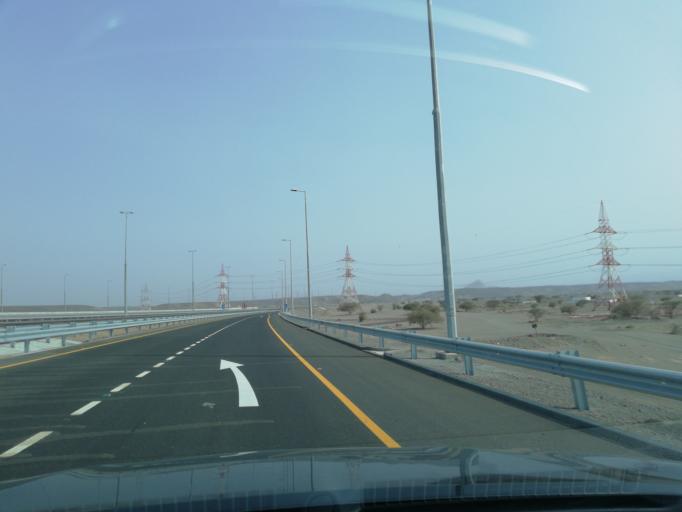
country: OM
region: Al Batinah
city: Al Liwa'
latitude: 24.3789
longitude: 56.5539
